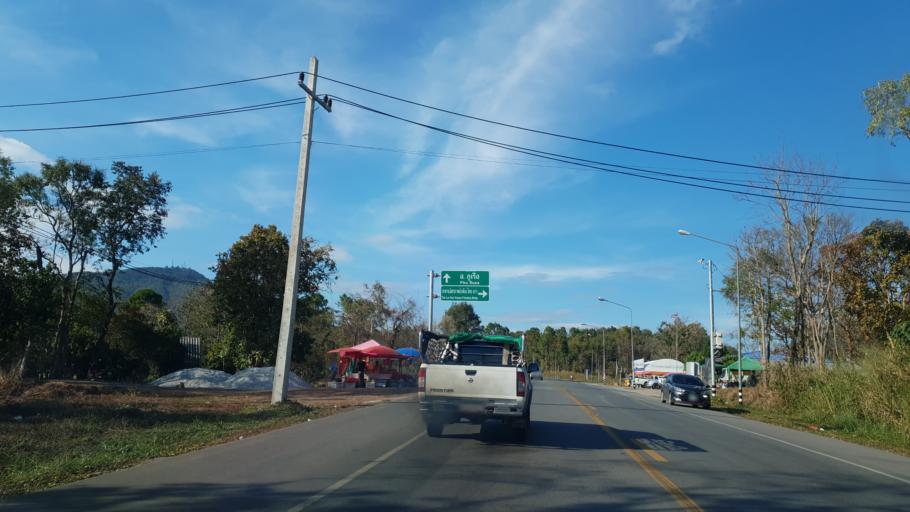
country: TH
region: Loei
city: Phu Ruea
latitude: 17.4447
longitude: 101.4672
